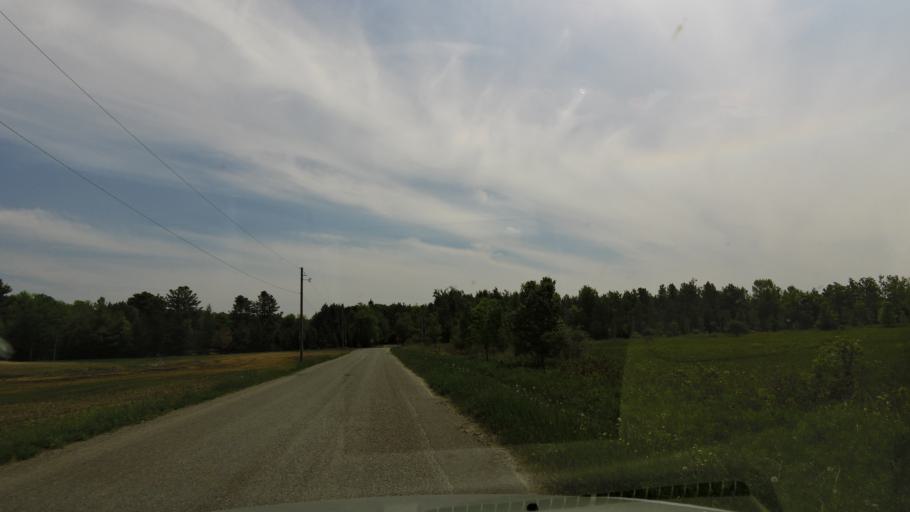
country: CA
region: Ontario
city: Cobourg
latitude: 43.9820
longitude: -78.4784
